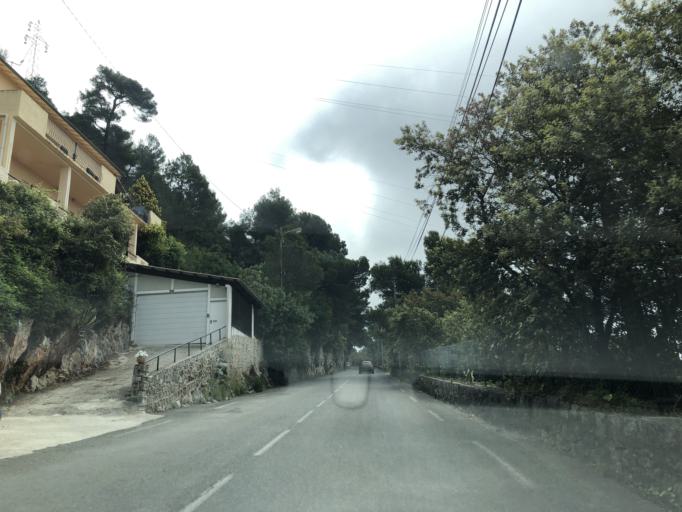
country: FR
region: Provence-Alpes-Cote d'Azur
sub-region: Departement des Alpes-Maritimes
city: Villefranche-sur-Mer
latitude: 43.7170
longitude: 7.3168
